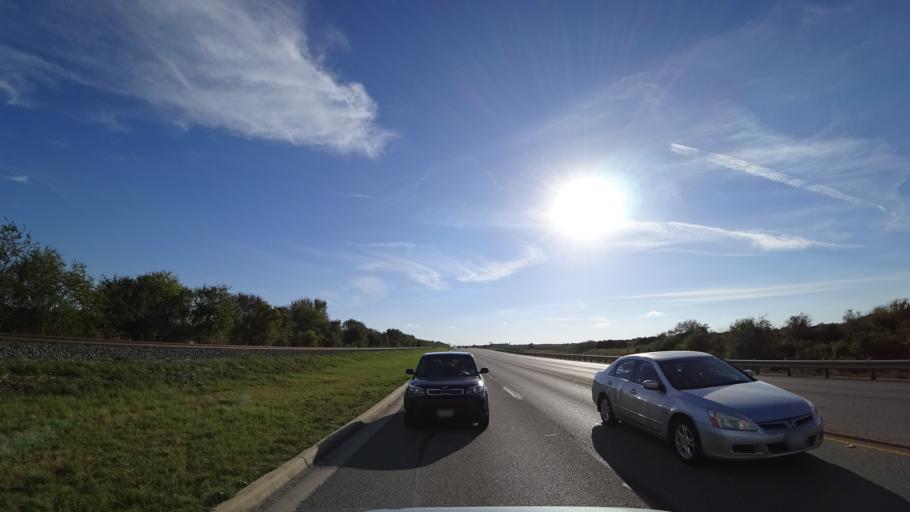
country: US
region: Texas
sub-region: Travis County
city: Wells Branch
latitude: 30.4755
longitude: -97.7066
